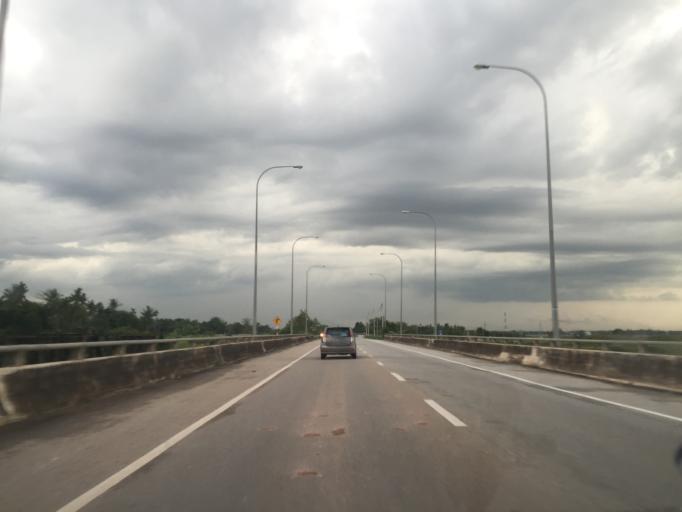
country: MY
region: Kedah
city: Sungai Petani
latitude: 5.5667
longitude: 100.5039
